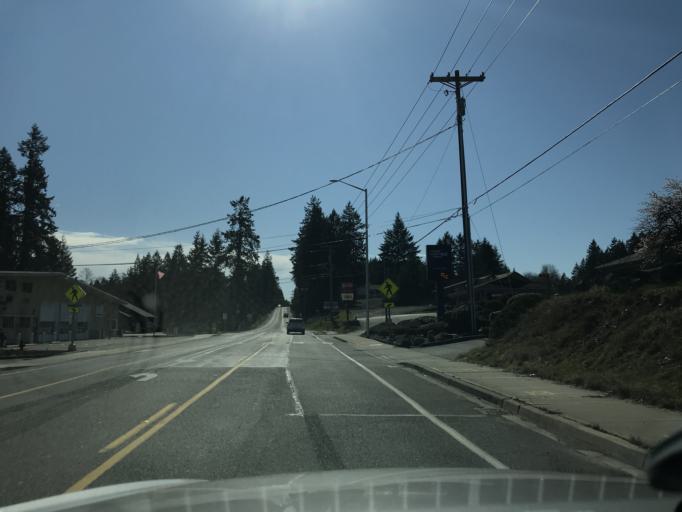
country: US
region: Washington
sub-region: Pierce County
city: Key Center
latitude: 47.3395
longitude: -122.7463
